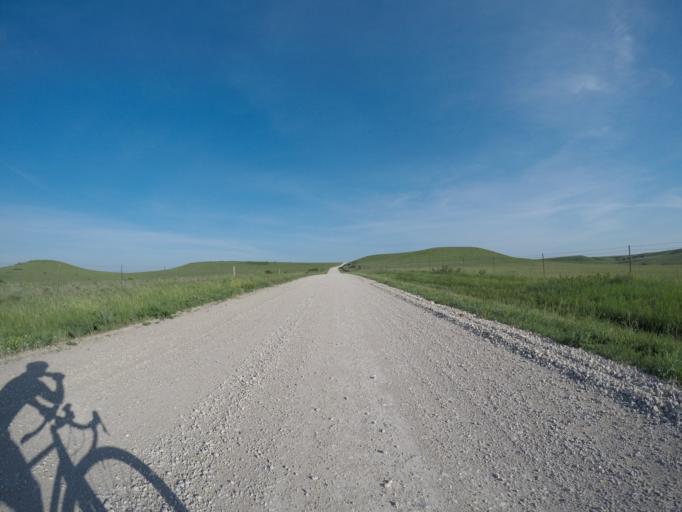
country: US
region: Kansas
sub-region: Riley County
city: Manhattan
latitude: 39.0429
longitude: -96.4927
